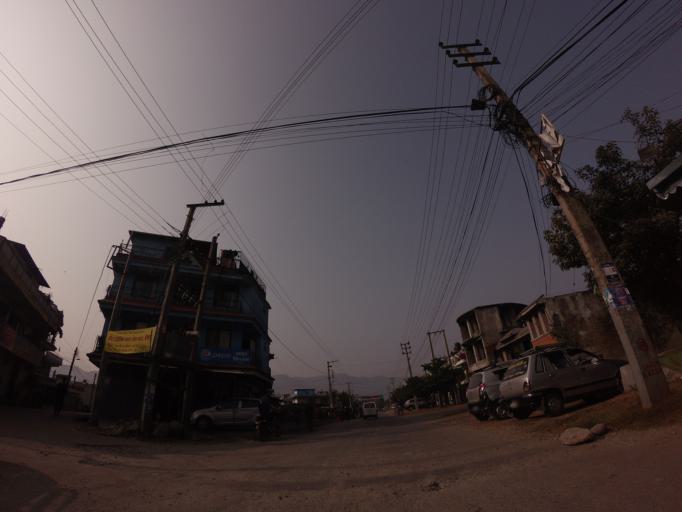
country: NP
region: Western Region
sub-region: Gandaki Zone
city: Pokhara
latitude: 28.1941
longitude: 83.9784
